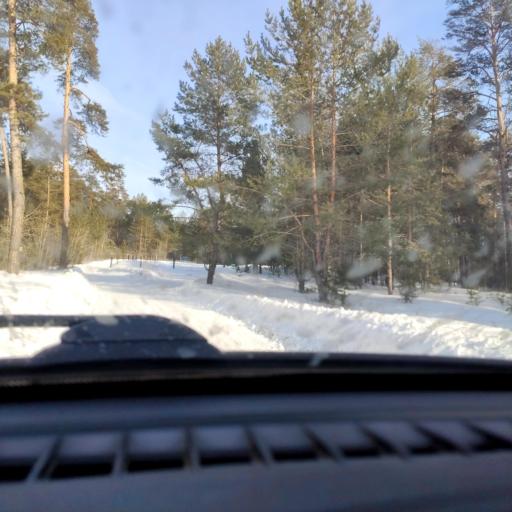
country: RU
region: Samara
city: Zhigulevsk
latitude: 53.4795
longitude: 49.5433
